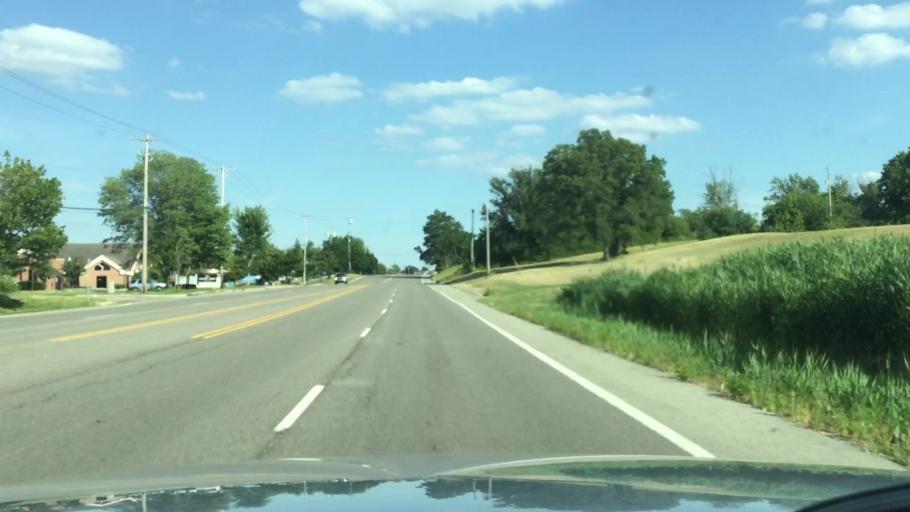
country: US
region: Michigan
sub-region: Genesee County
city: Grand Blanc
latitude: 42.9140
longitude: -83.6115
